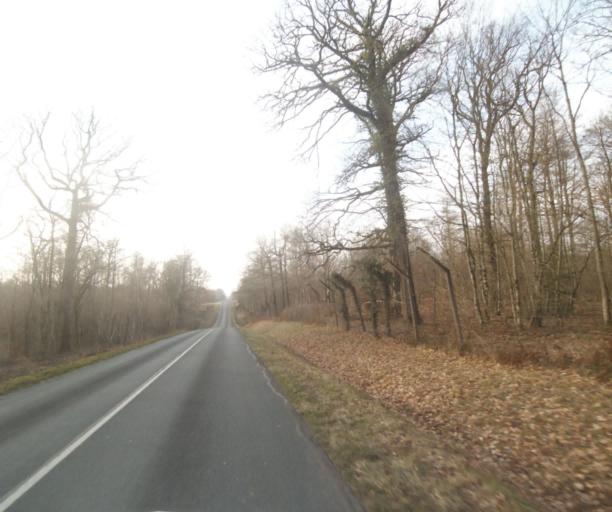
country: FR
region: Champagne-Ardenne
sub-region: Departement de la Haute-Marne
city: Chancenay
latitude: 48.6899
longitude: 4.9449
